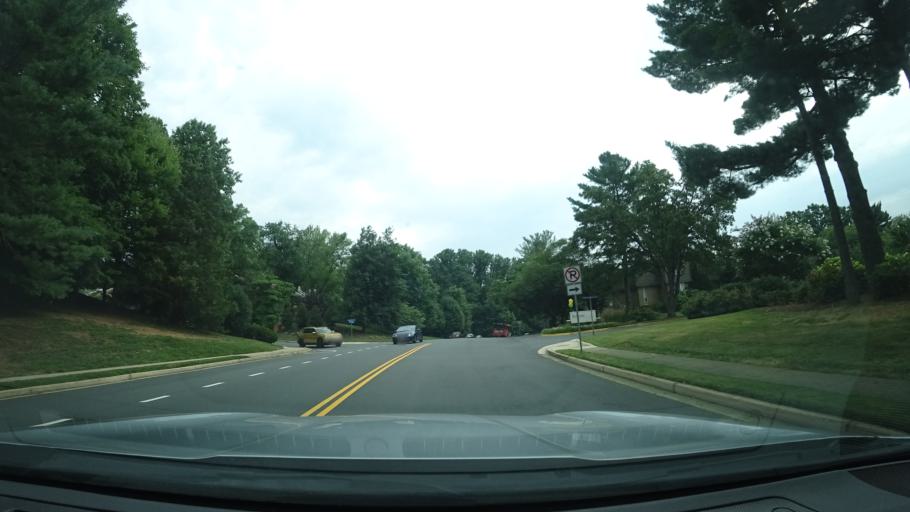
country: US
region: Virginia
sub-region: Fairfax County
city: Reston
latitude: 38.9628
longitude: -77.3509
